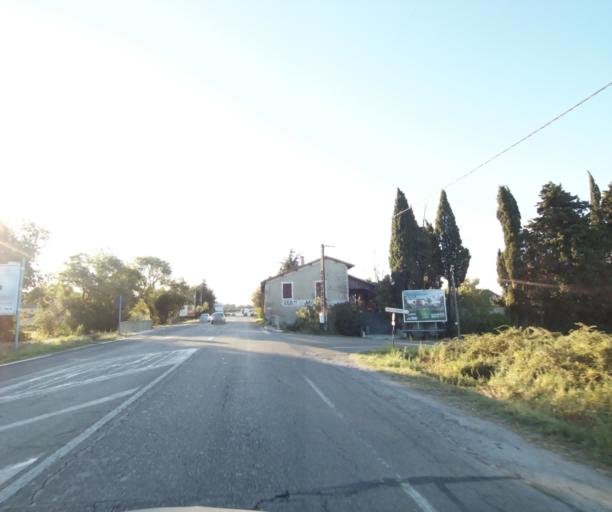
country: FR
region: Languedoc-Roussillon
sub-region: Departement du Gard
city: Caissargues
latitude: 43.8145
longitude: 4.3963
